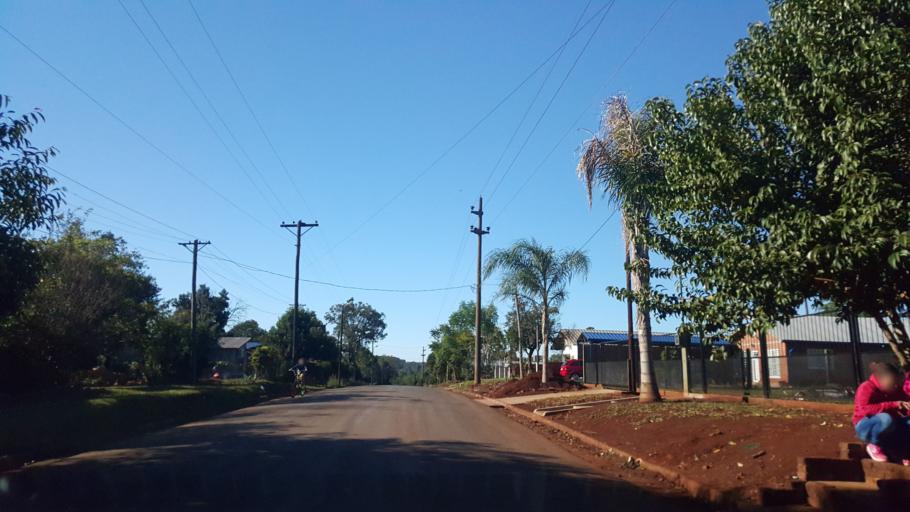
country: AR
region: Misiones
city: Gobernador Roca
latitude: -27.1819
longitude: -55.4583
